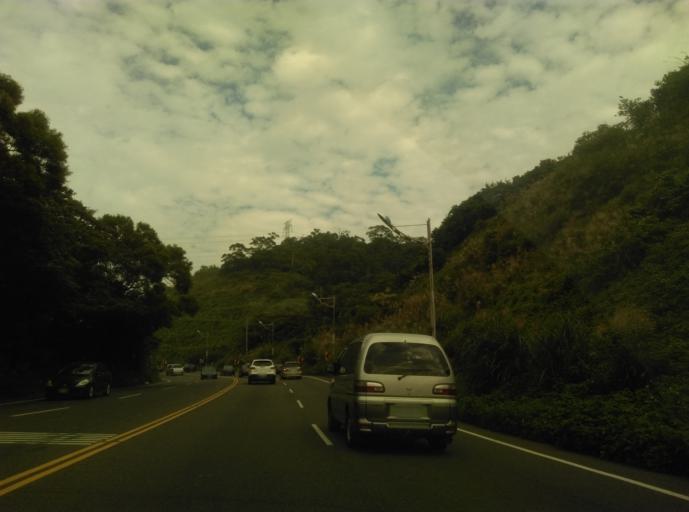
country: TW
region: Taiwan
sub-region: Keelung
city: Keelung
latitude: 25.1567
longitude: 121.6969
